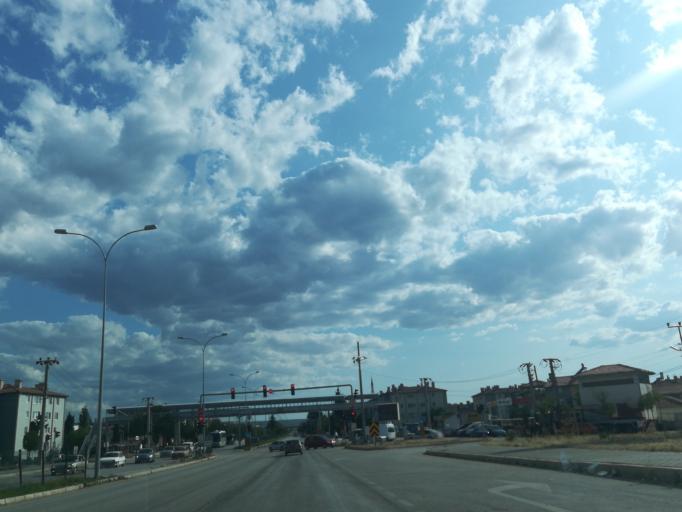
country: TR
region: Afyonkarahisar
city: Dinar
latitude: 38.0651
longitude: 30.1657
